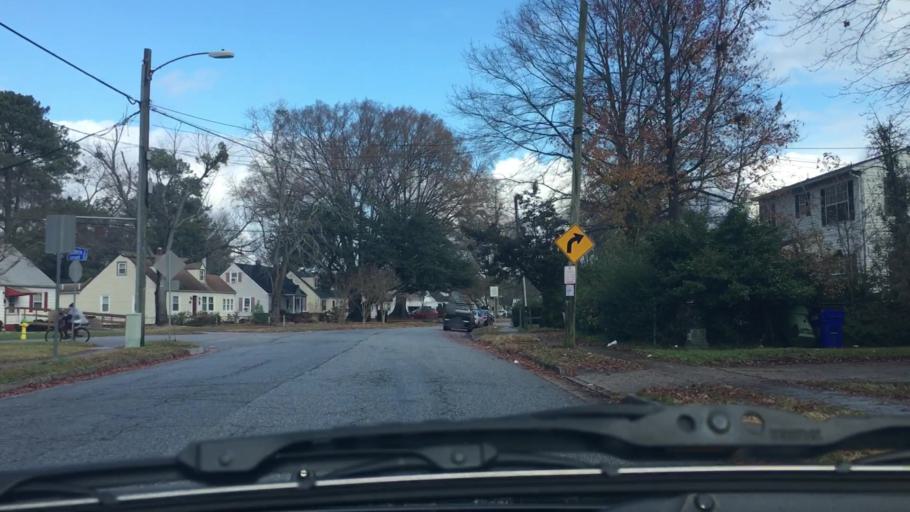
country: US
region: Virginia
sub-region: City of Norfolk
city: Norfolk
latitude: 36.9189
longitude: -76.2499
